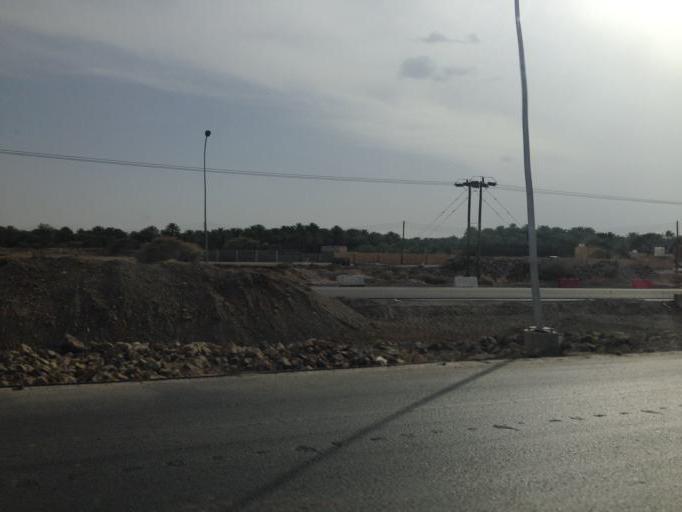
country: OM
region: Ash Sharqiyah
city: Al Qabil
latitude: 22.5687
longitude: 58.7003
